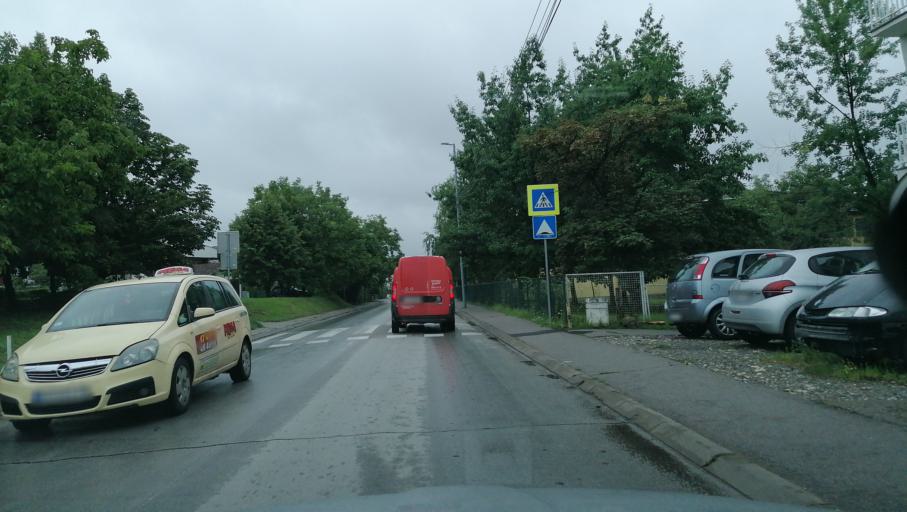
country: RS
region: Central Serbia
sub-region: Rasinski Okrug
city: Krusevac
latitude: 43.5759
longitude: 21.3269
